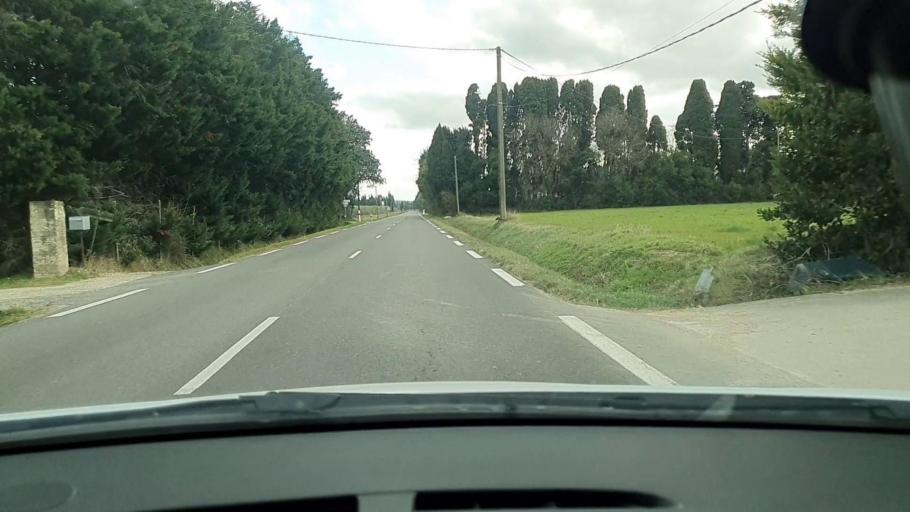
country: FR
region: Languedoc-Roussillon
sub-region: Departement du Gard
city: Meynes
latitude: 43.8946
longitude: 4.5730
